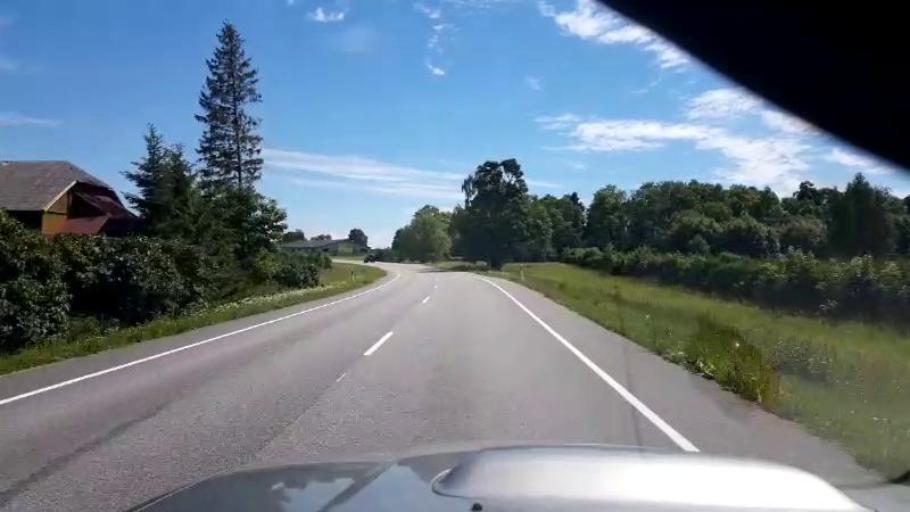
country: EE
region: Jaervamaa
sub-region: Jaerva-Jaani vald
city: Jarva-Jaani
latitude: 59.0037
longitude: 25.9313
